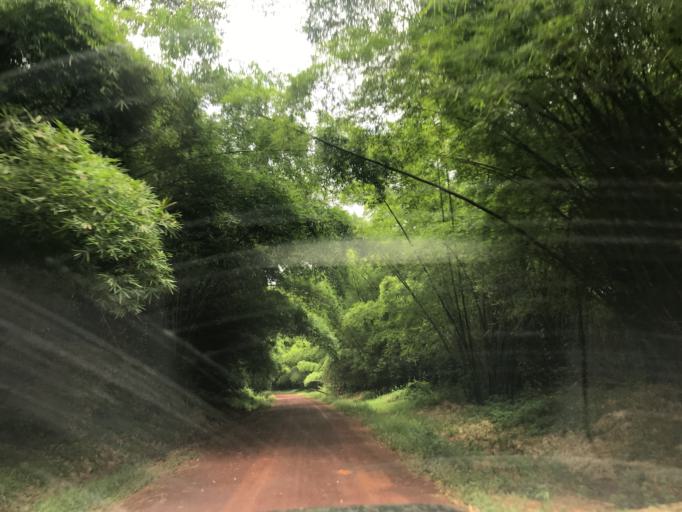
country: CD
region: Eastern Province
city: Buta
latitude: 2.4011
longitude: 24.9147
